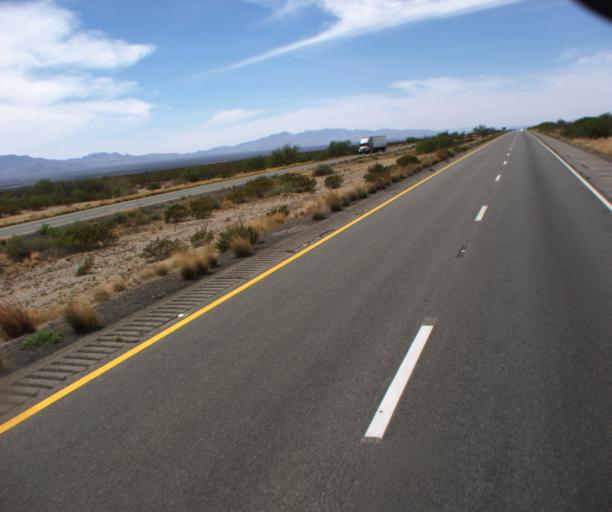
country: US
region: New Mexico
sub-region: Hidalgo County
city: Lordsburg
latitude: 32.2408
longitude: -109.1058
